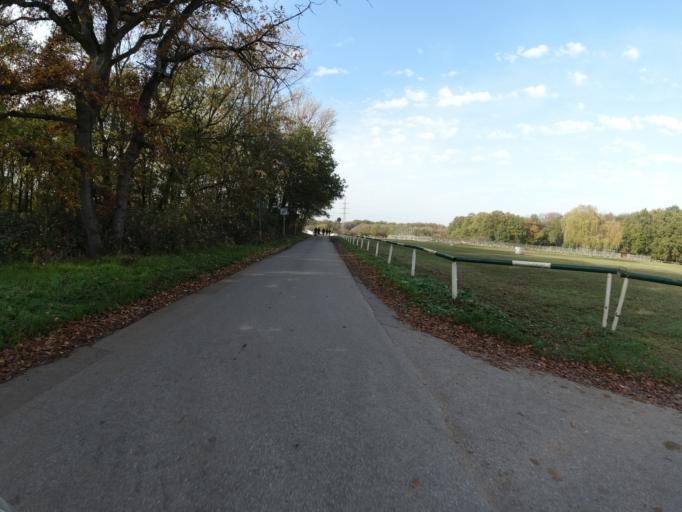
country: DE
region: North Rhine-Westphalia
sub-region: Regierungsbezirk Dusseldorf
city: Moers
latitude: 51.4061
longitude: 6.6466
